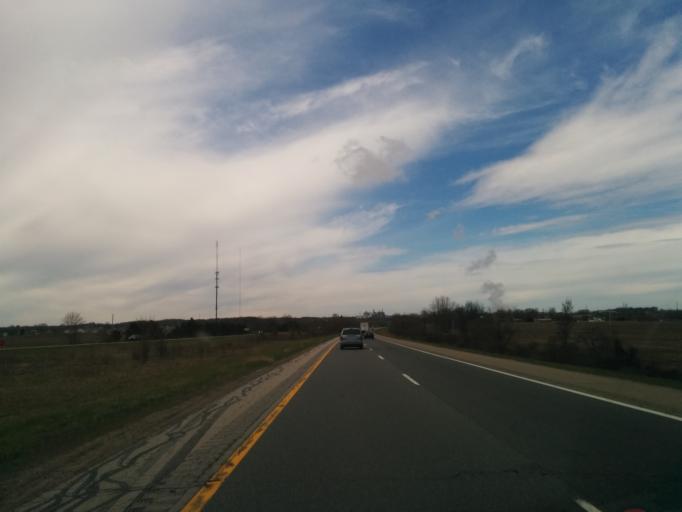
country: US
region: Michigan
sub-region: Ottawa County
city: Zeeland
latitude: 42.8197
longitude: -85.9467
